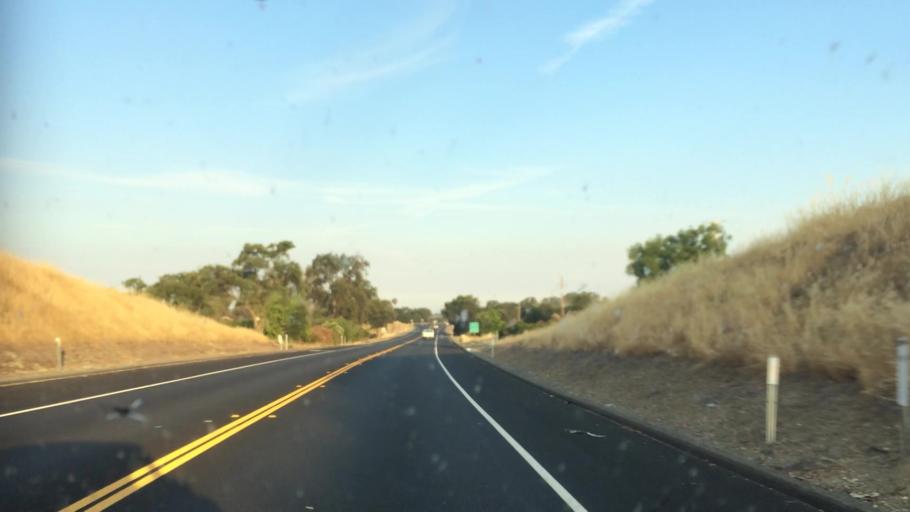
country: US
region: California
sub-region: Amador County
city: Plymouth
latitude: 38.4495
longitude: -120.8911
